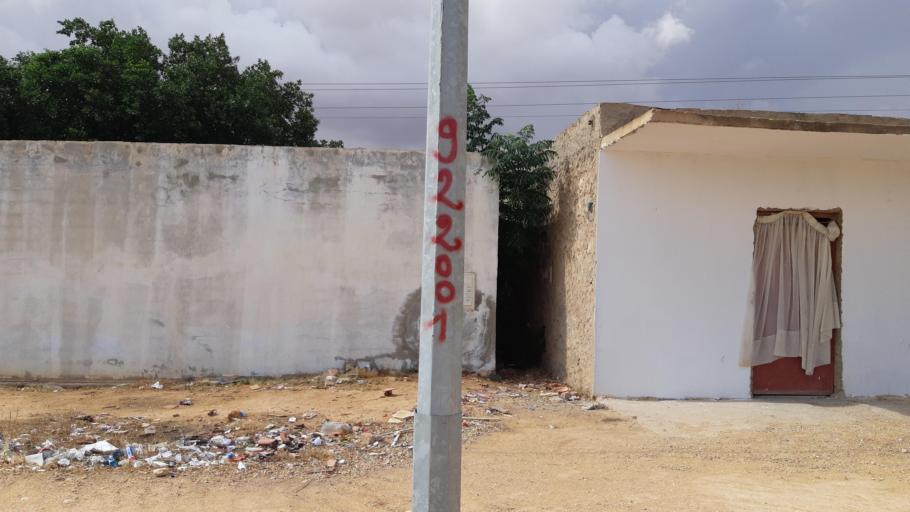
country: TN
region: Safaqis
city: Sfax
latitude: 34.7603
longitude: 10.6261
